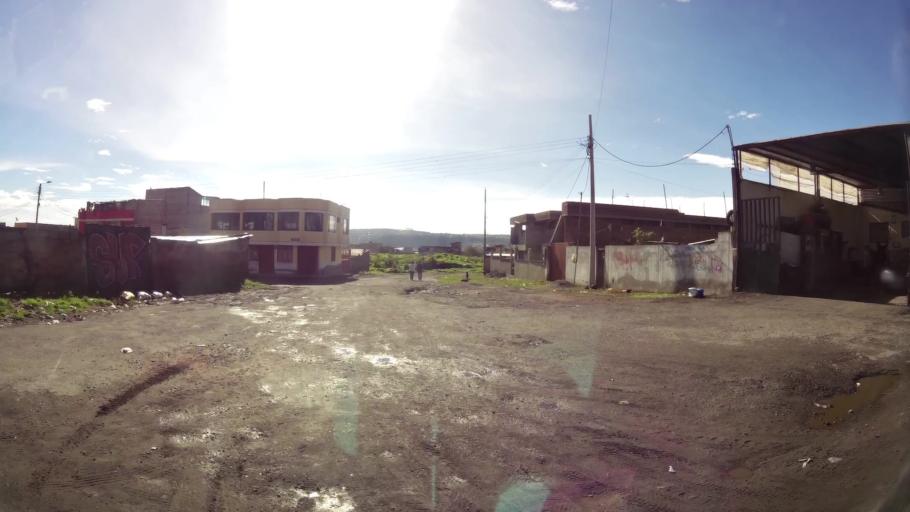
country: EC
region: Pichincha
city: Quito
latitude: -0.3192
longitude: -78.5573
